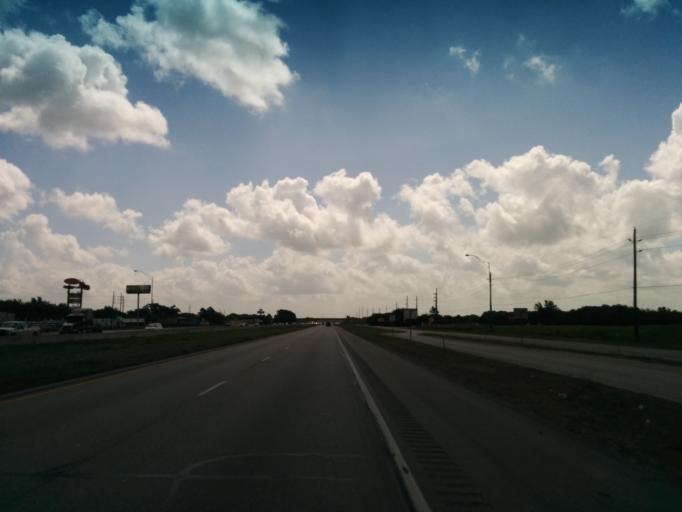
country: US
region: Texas
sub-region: Austin County
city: Sealy
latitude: 29.7757
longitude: -96.1161
